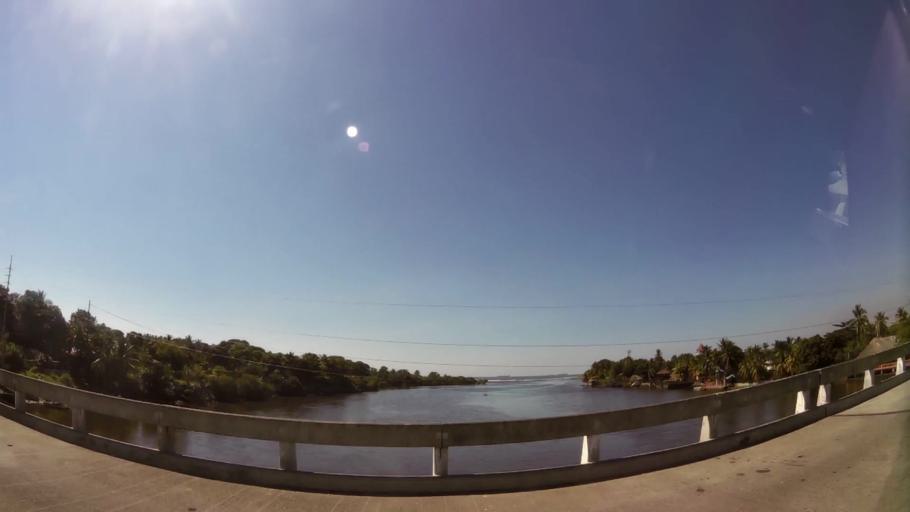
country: GT
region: Escuintla
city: Iztapa
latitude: 13.9327
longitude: -90.7074
